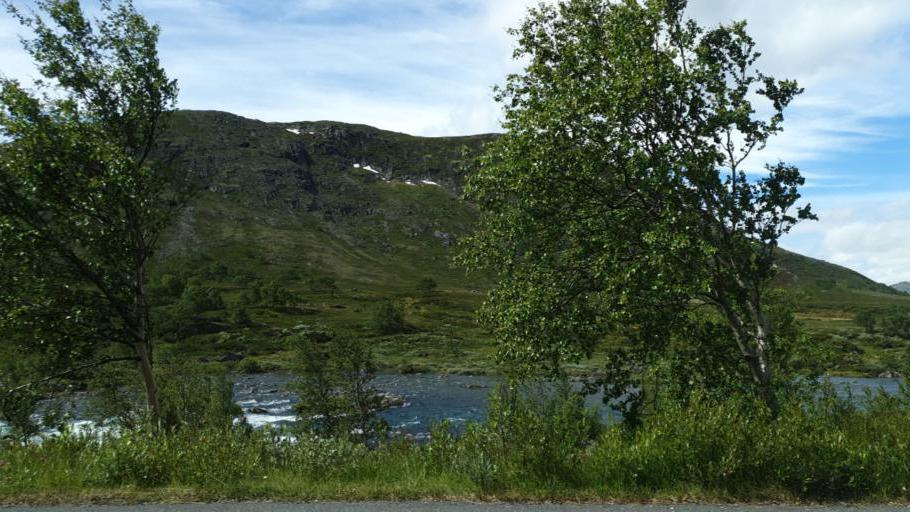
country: NO
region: Oppland
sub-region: Lom
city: Fossbergom
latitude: 61.4917
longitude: 8.8169
